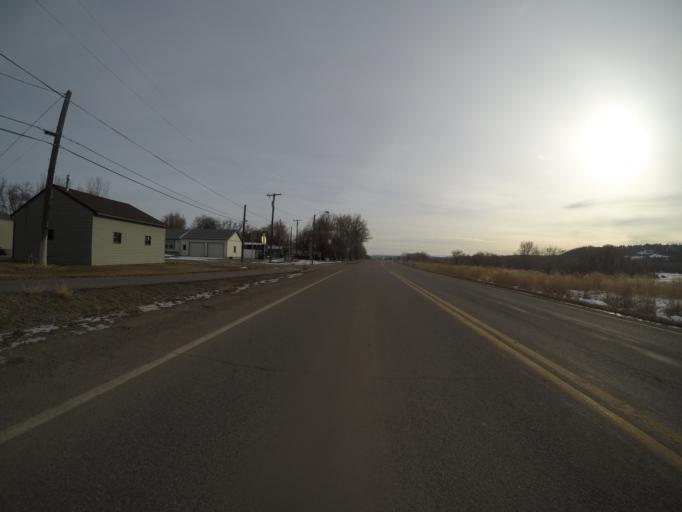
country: US
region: Montana
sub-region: Stillwater County
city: Columbus
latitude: 45.6397
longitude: -109.2632
